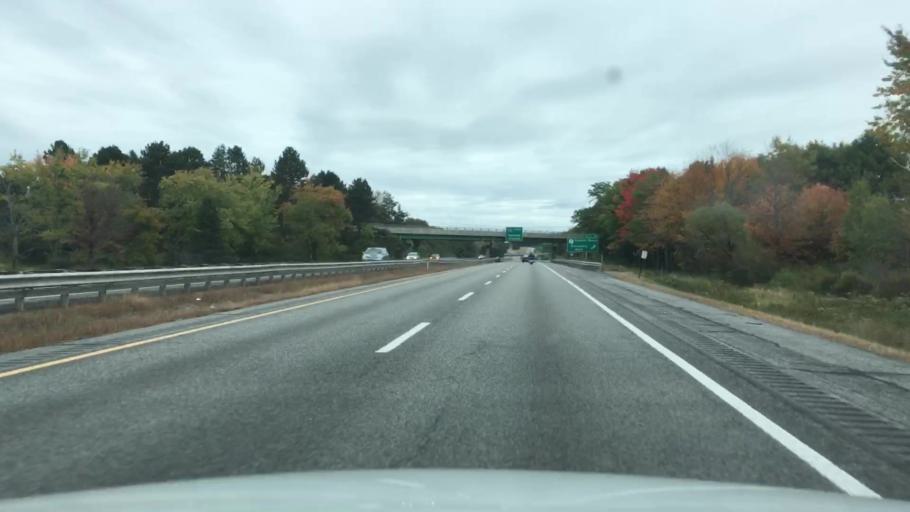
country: US
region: Maine
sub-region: Sagadahoc County
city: Topsham
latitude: 43.9141
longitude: -70.0312
